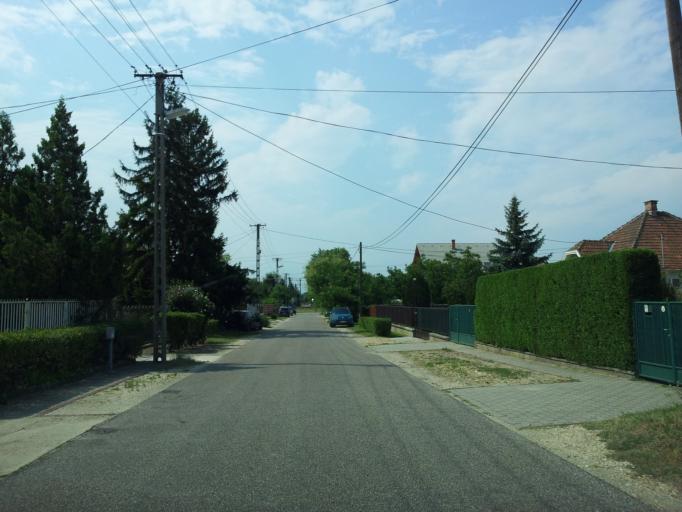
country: HU
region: Pest
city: Szigethalom
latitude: 47.3314
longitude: 19.0000
